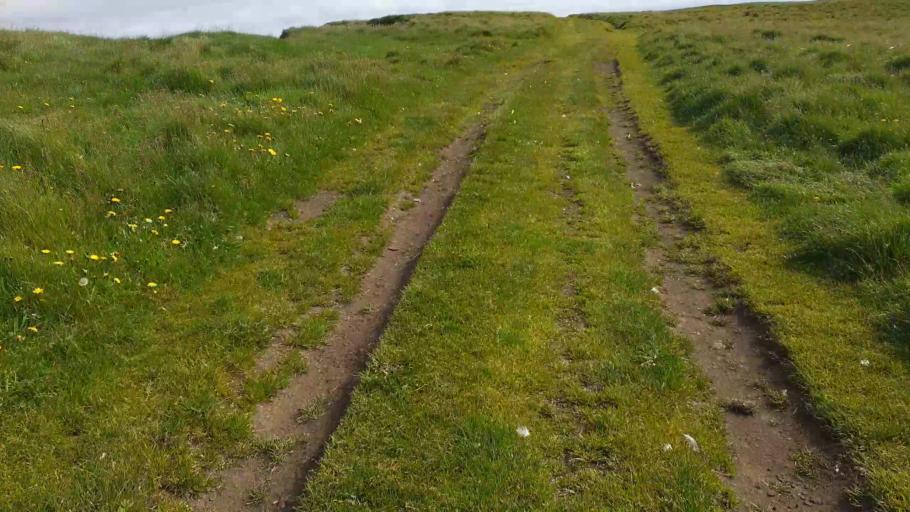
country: IS
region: Northeast
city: Dalvik
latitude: 66.5523
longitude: -17.9964
